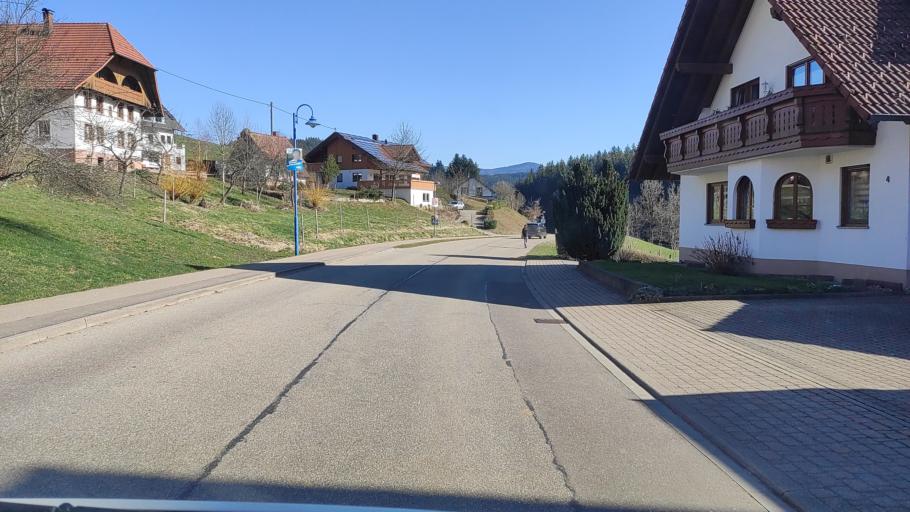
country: DE
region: Baden-Wuerttemberg
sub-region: Freiburg Region
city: Elzach
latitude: 48.1938
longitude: 8.0353
